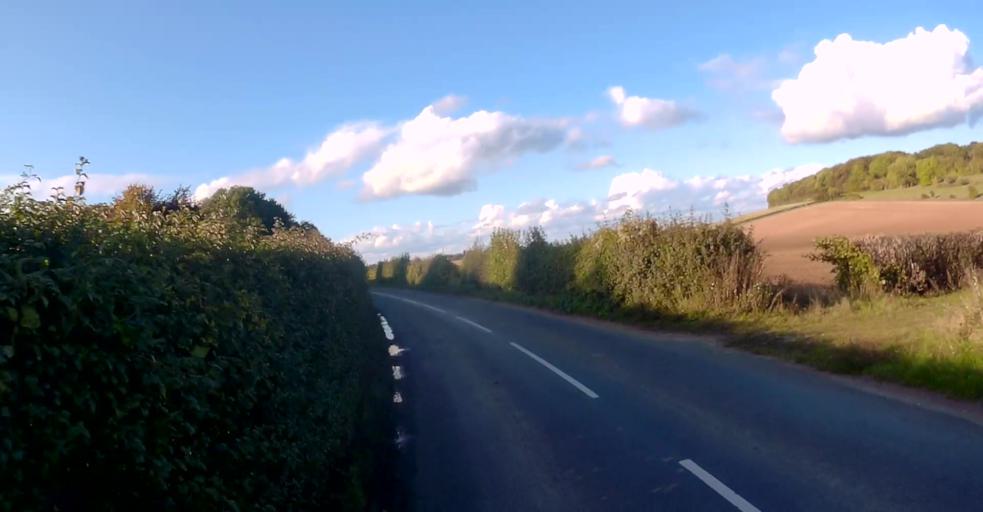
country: GB
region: England
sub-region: Hampshire
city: Odiham
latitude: 51.2379
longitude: -0.9257
